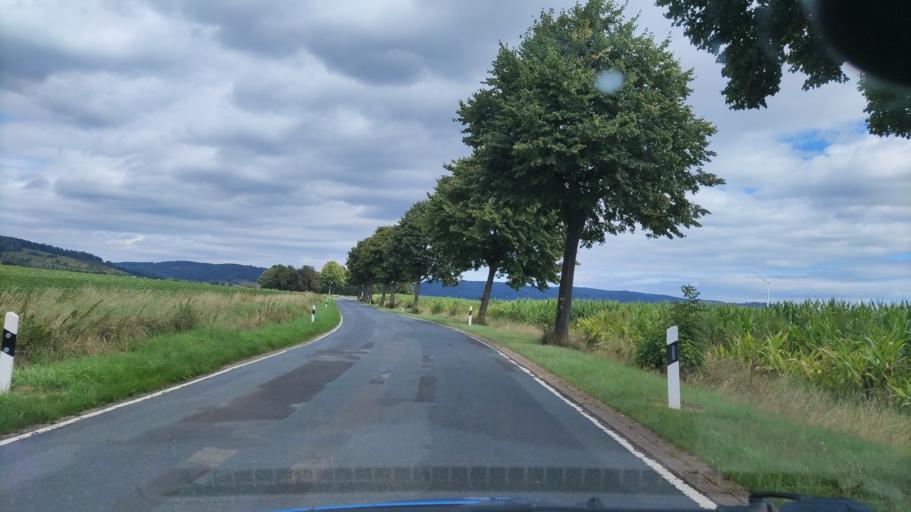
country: DE
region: Lower Saxony
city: Dassel
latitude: 51.8276
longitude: 9.7180
